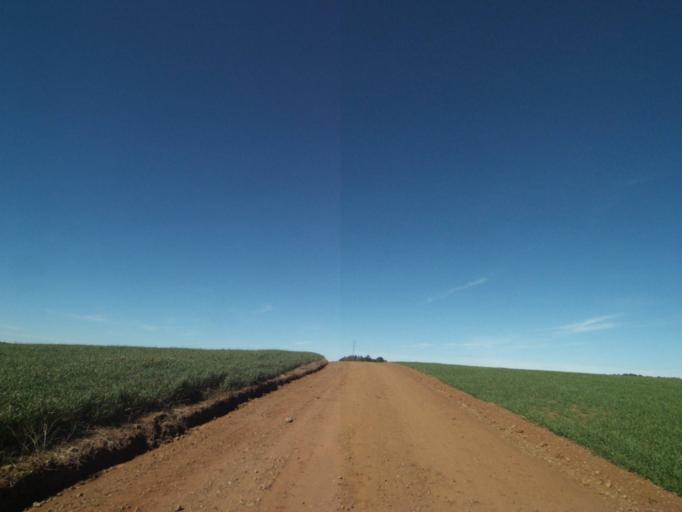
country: BR
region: Parana
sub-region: Tibagi
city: Tibagi
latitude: -24.5733
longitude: -50.2659
